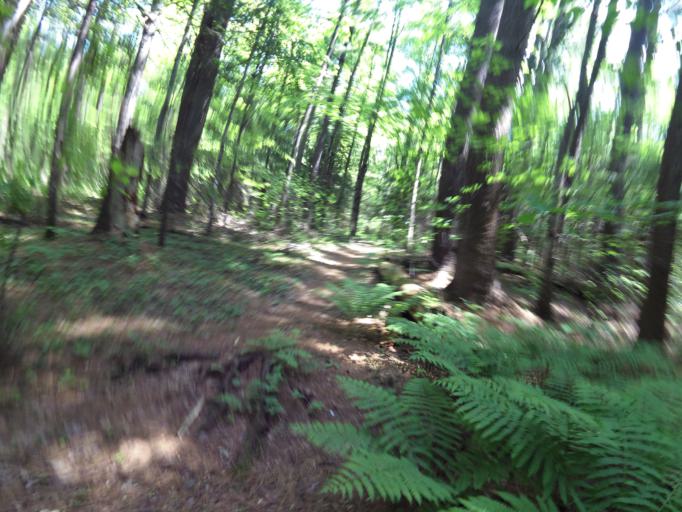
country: CA
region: Ontario
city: Ottawa
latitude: 45.3556
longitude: -75.6036
